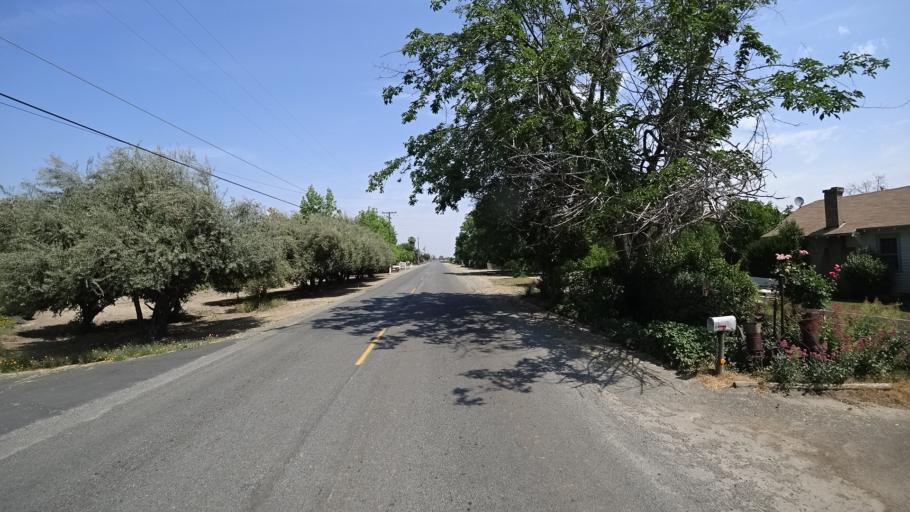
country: US
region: California
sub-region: Kings County
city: Lemoore
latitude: 36.3186
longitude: -119.7628
